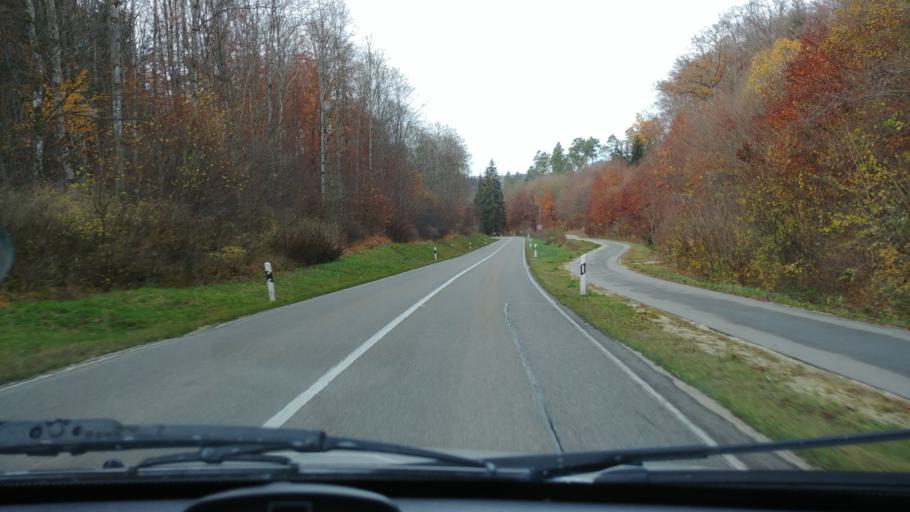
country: DE
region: Baden-Wuerttemberg
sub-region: Regierungsbezirk Stuttgart
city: Herbrechtingen
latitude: 48.6631
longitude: 10.2033
